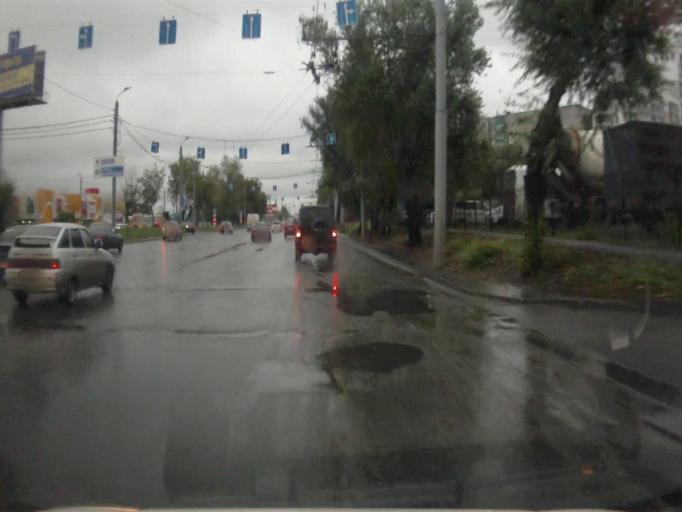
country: RU
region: Chelyabinsk
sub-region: Gorod Chelyabinsk
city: Chelyabinsk
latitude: 55.1452
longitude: 61.4477
